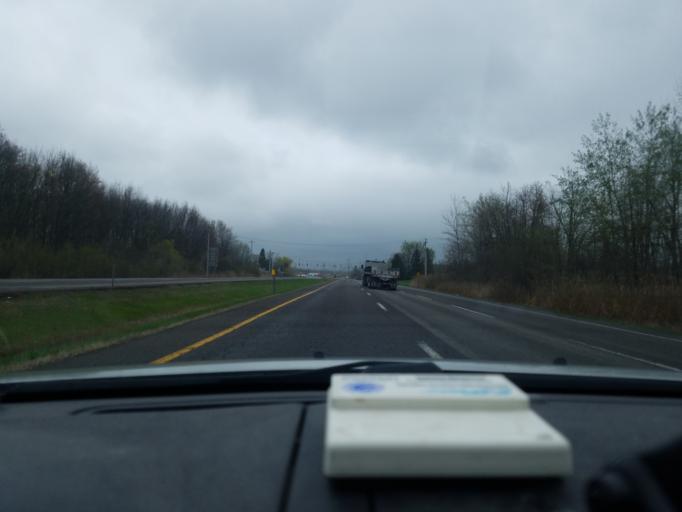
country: US
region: New York
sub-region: Onondaga County
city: North Syracuse
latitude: 43.1336
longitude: -76.0821
